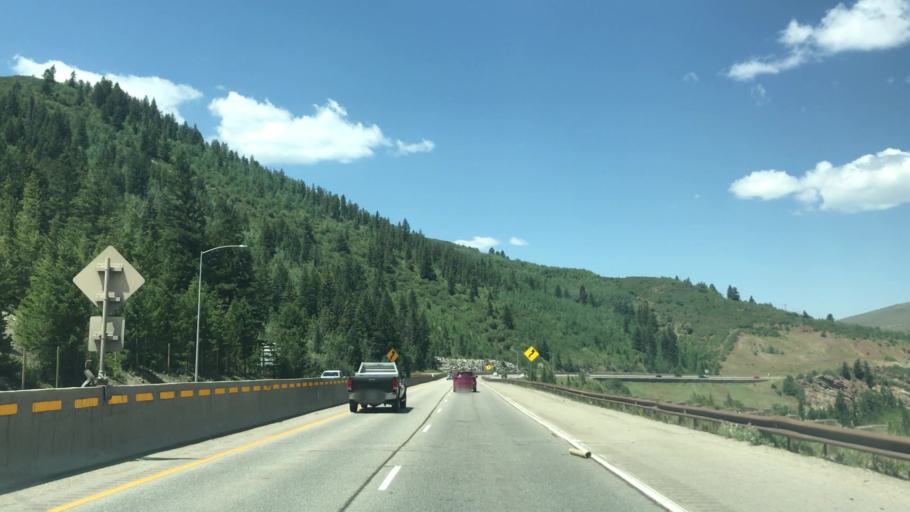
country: US
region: Colorado
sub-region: Eagle County
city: Minturn
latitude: 39.6090
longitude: -106.4529
